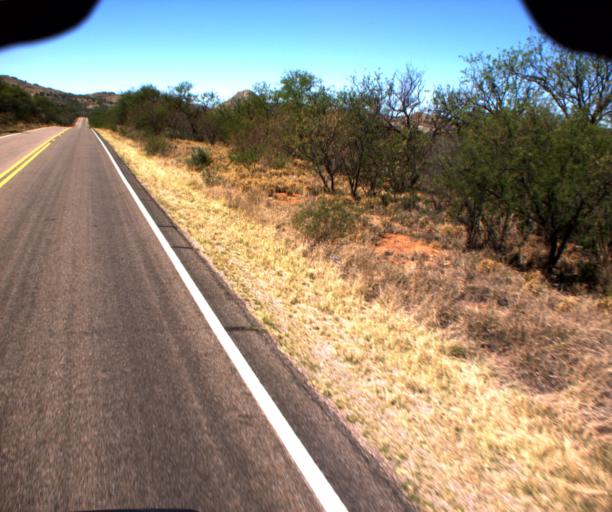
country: US
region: Arizona
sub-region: Santa Cruz County
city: Rio Rico
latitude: 31.5242
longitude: -110.7731
